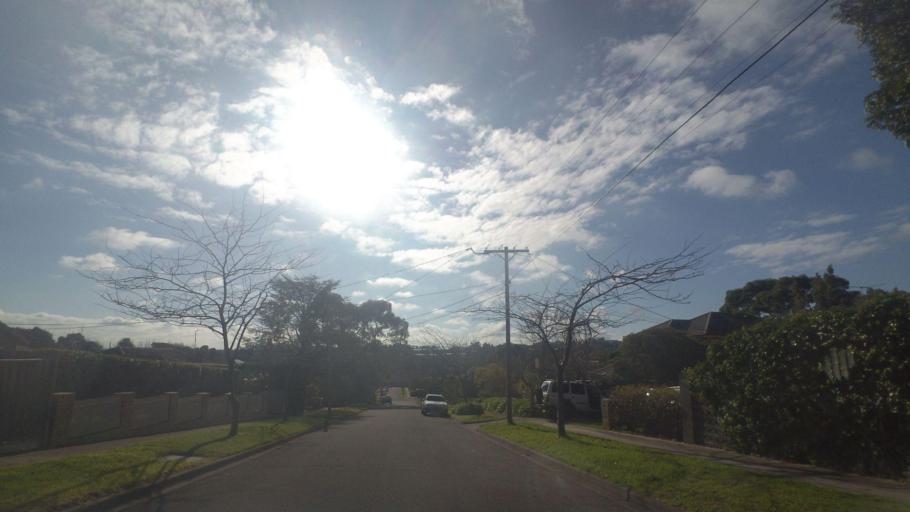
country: AU
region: Victoria
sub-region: Whitehorse
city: Mont Albert North
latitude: -37.7990
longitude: 145.1123
